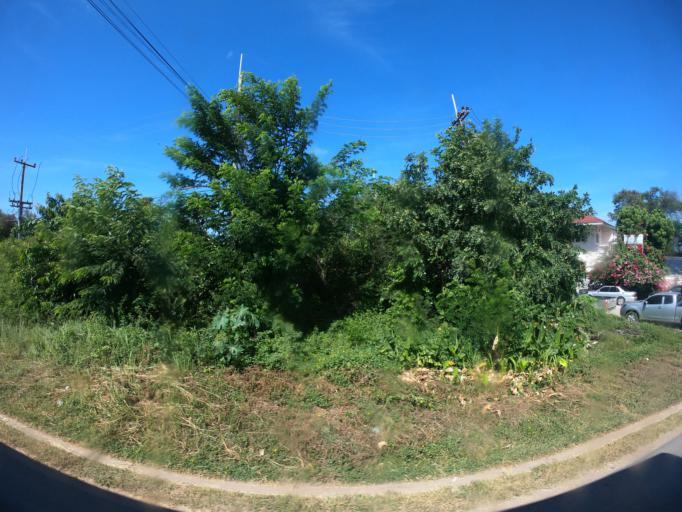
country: TH
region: Nakhon Ratchasima
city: Nakhon Ratchasima
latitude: 15.0515
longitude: 102.1563
